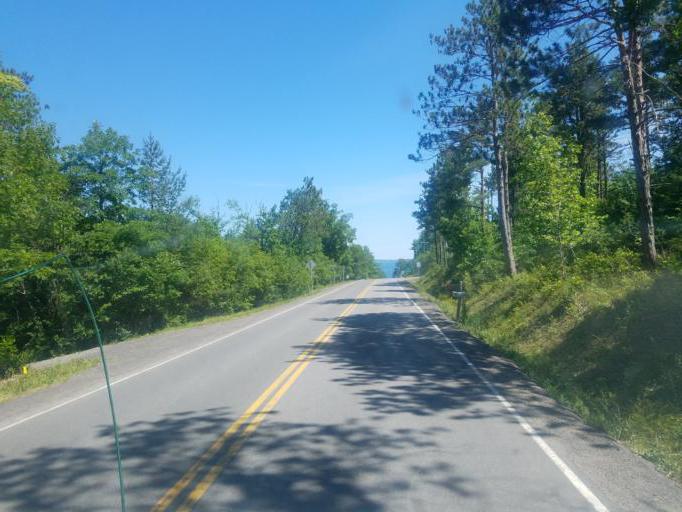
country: US
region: New York
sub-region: Ontario County
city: Canandaigua
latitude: 42.7606
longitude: -77.2994
